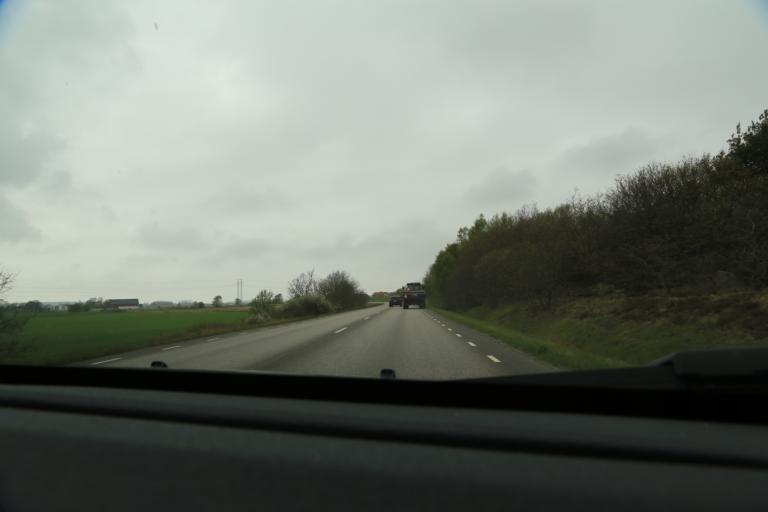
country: SE
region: Halland
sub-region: Kungsbacka Kommun
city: Frillesas
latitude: 57.2375
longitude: 12.1770
